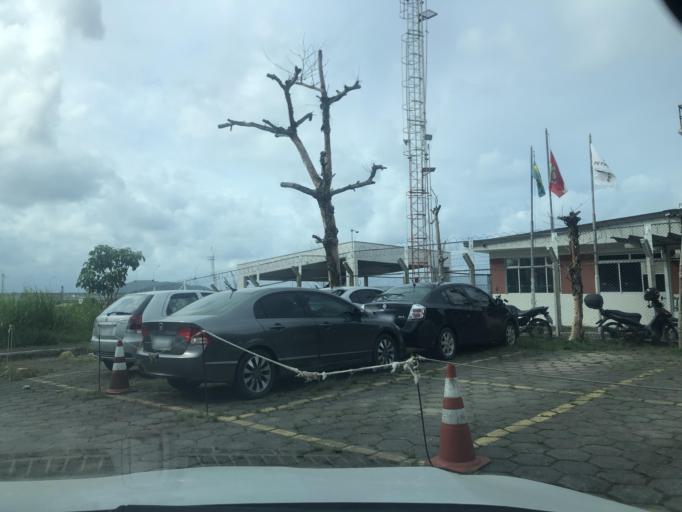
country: BR
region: Santa Catarina
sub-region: Sao Francisco Do Sul
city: Sao Francisco do Sul
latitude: -26.2198
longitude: -48.4986
